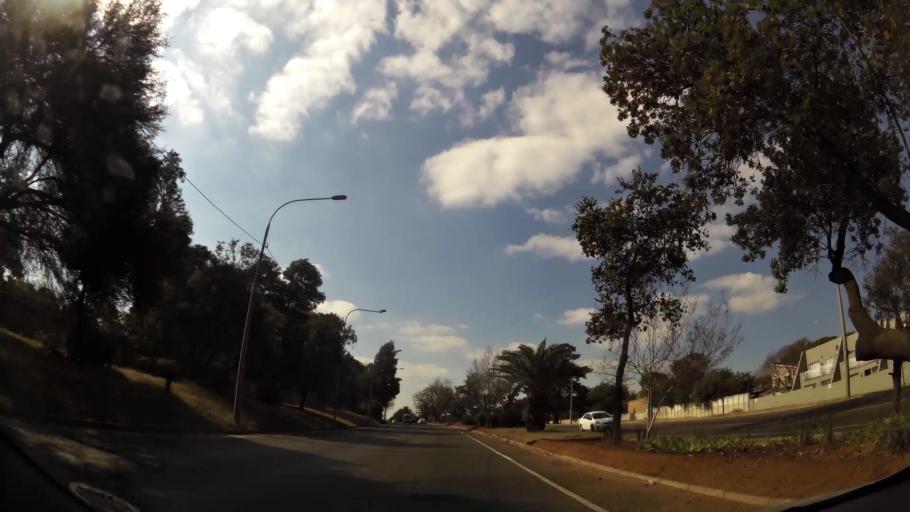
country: ZA
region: Gauteng
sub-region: West Rand District Municipality
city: Krugersdorp
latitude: -26.0865
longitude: 27.7865
